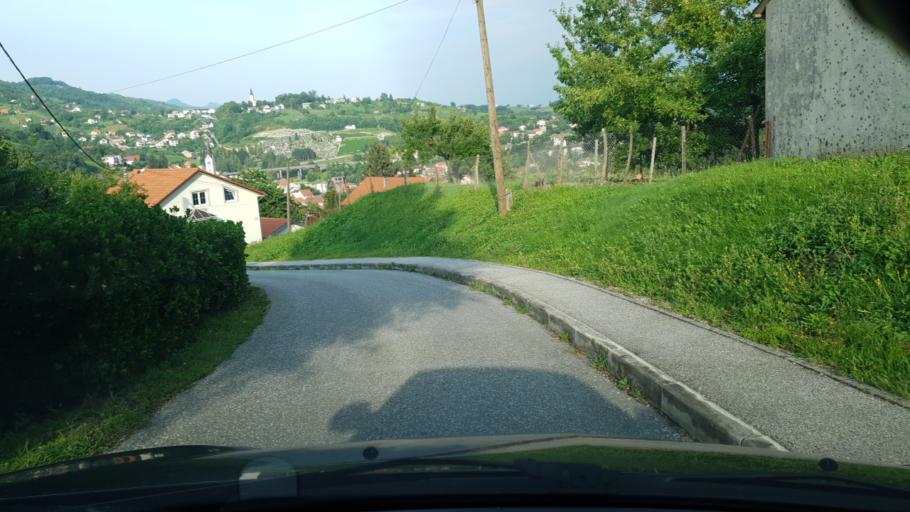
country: HR
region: Krapinsko-Zagorska
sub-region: Grad Krapina
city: Krapina
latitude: 46.1621
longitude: 15.8639
